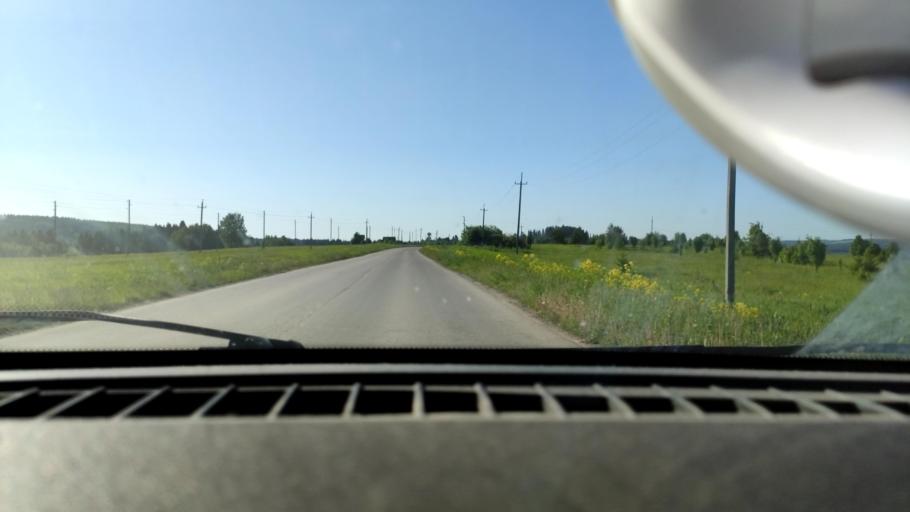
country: RU
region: Perm
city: Novyye Lyady
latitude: 58.1809
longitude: 56.5533
